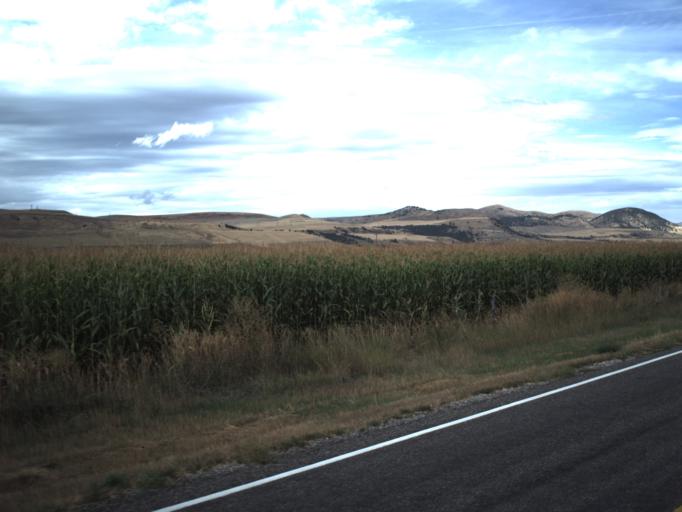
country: US
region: Utah
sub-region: Cache County
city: Lewiston
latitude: 41.9300
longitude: -111.9532
